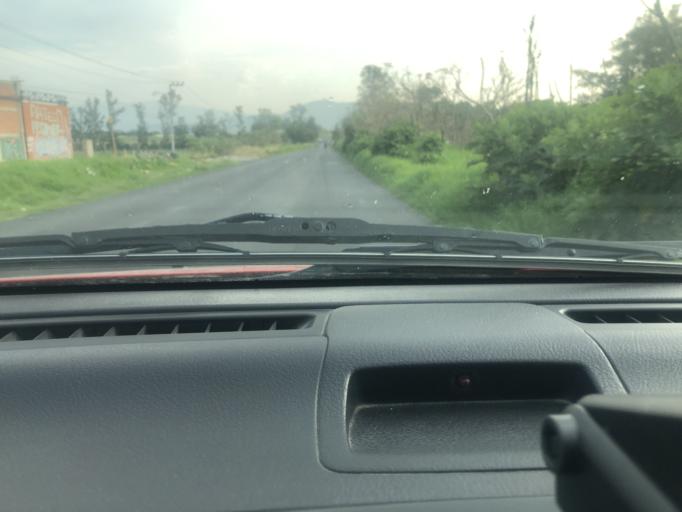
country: MX
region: Jalisco
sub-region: San Pedro Tlaquepaque
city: Paseo del Prado
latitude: 20.5724
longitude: -103.4060
